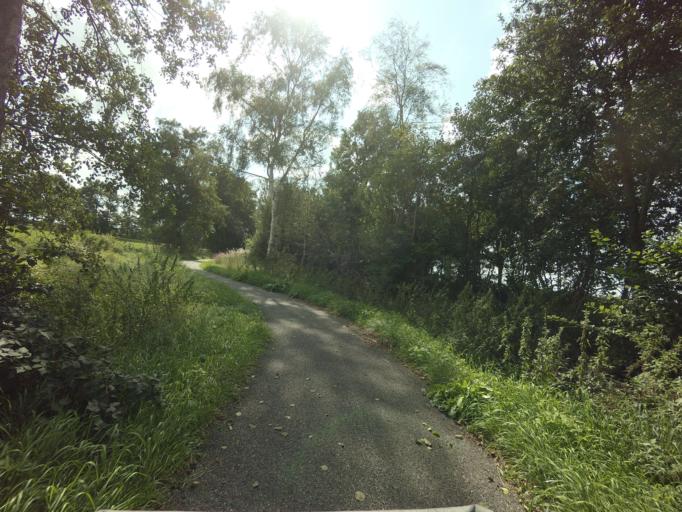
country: NL
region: Drenthe
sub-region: Gemeente Westerveld
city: Dwingeloo
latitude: 52.8573
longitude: 6.4659
